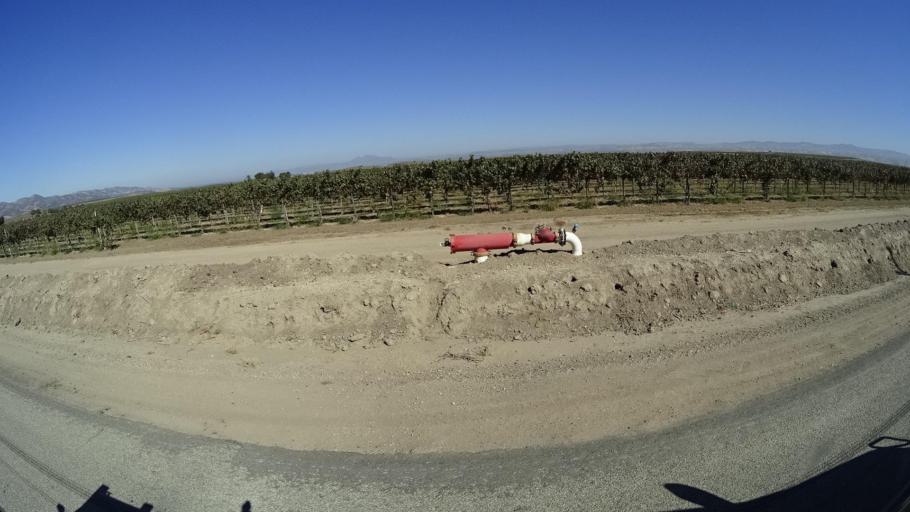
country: US
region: California
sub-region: Monterey County
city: King City
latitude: 36.1395
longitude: -121.0963
